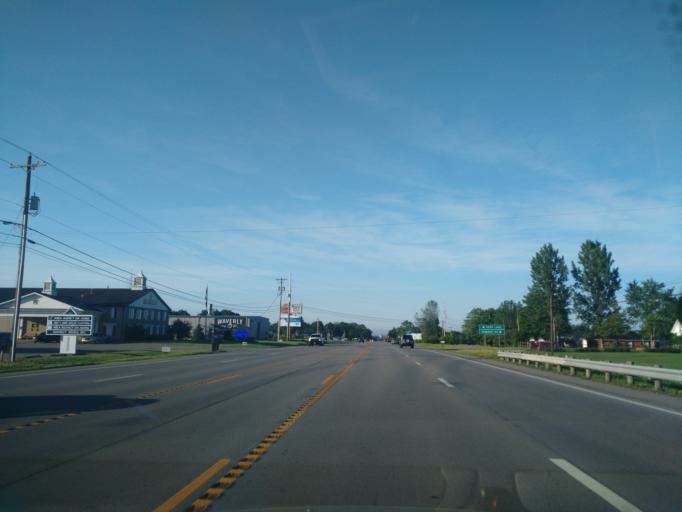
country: US
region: Ohio
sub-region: Pike County
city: Waverly
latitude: 39.1497
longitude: -82.9772
